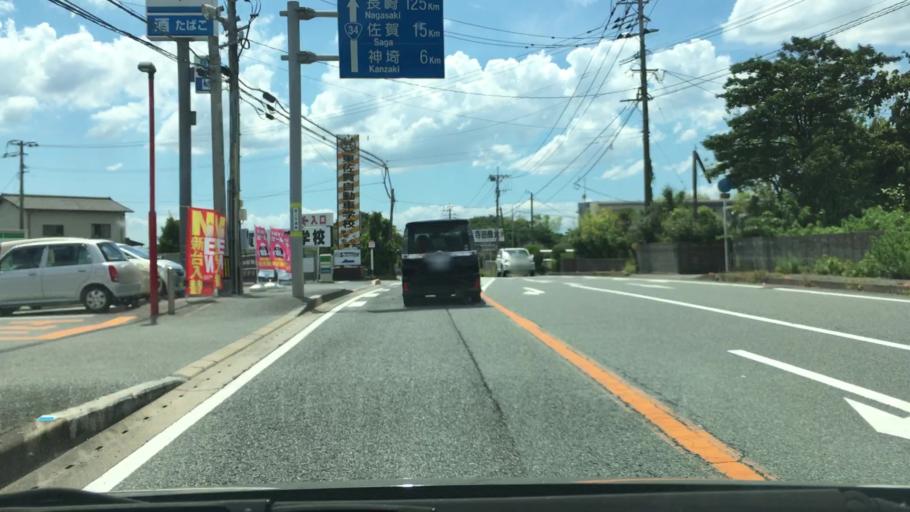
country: JP
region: Saga Prefecture
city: Kanzakimachi-kanzaki
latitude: 33.3359
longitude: 130.4184
